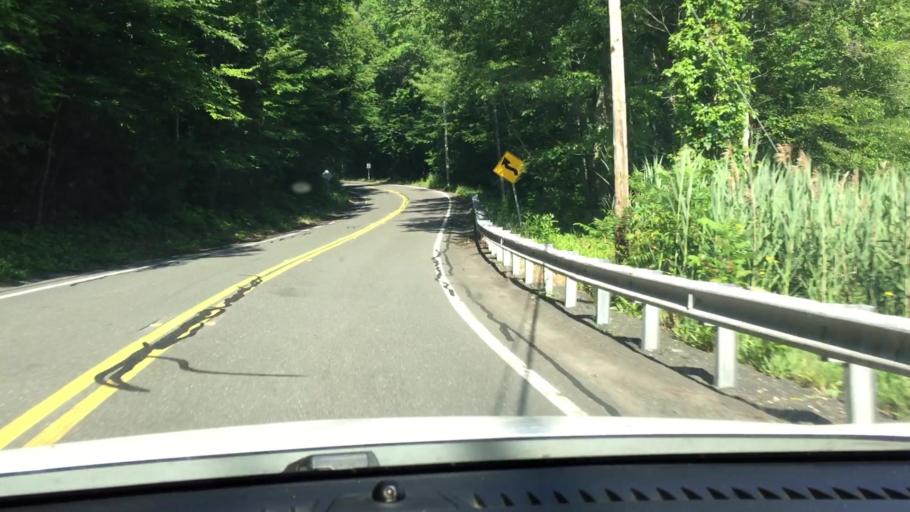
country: US
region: Massachusetts
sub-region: Berkshire County
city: Otis
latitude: 42.1731
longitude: -72.9760
